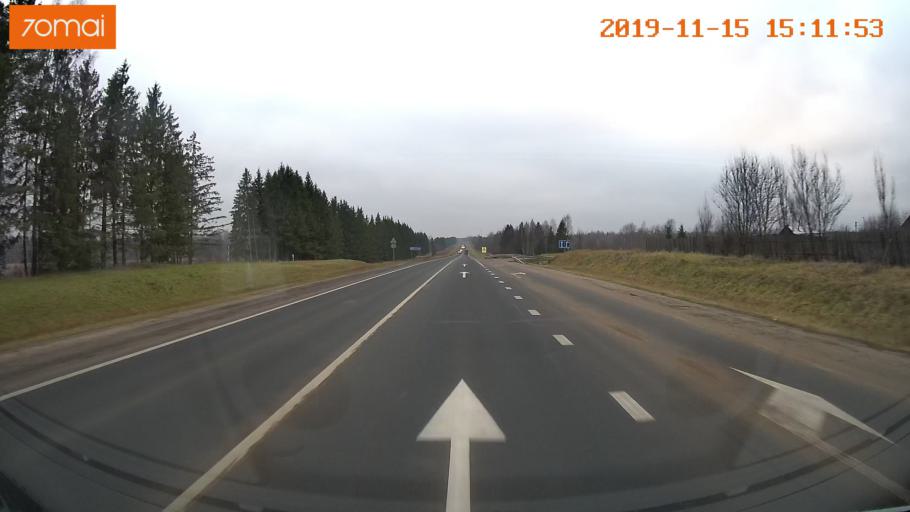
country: RU
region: Jaroslavl
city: Prechistoye
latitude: 58.3308
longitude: 40.2348
